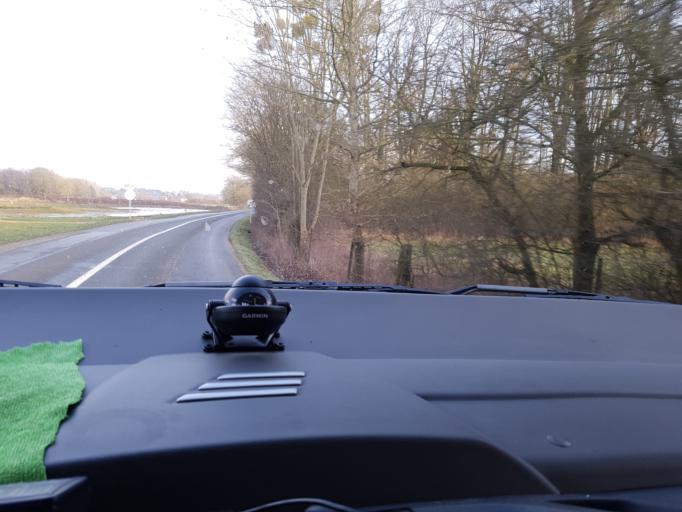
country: FR
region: Champagne-Ardenne
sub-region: Departement des Ardennes
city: Warcq
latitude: 49.7634
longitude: 4.6545
